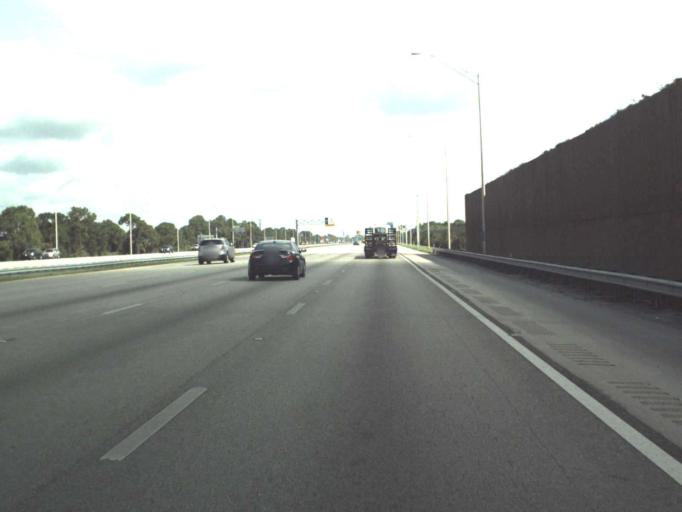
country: US
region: Florida
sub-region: Palm Beach County
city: Limestone Creek
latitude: 26.8987
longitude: -80.1366
